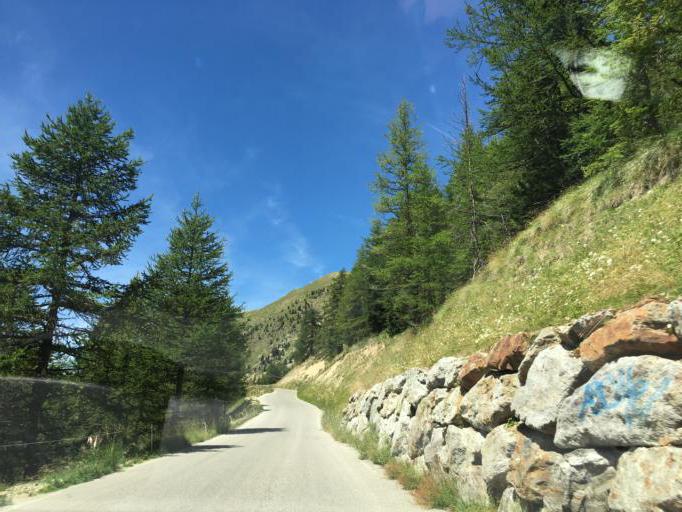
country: IT
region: Piedmont
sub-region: Provincia di Cuneo
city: Vinadio
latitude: 44.1916
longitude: 7.1571
